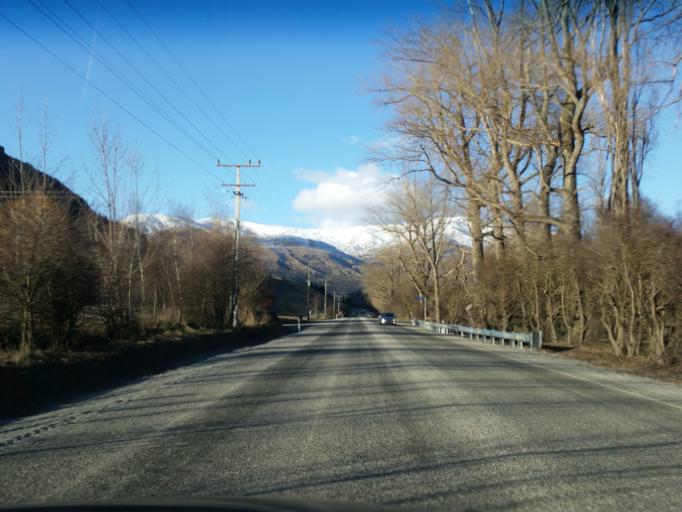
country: NZ
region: Otago
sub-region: Queenstown-Lakes District
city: Arrowtown
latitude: -44.9462
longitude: 168.7893
